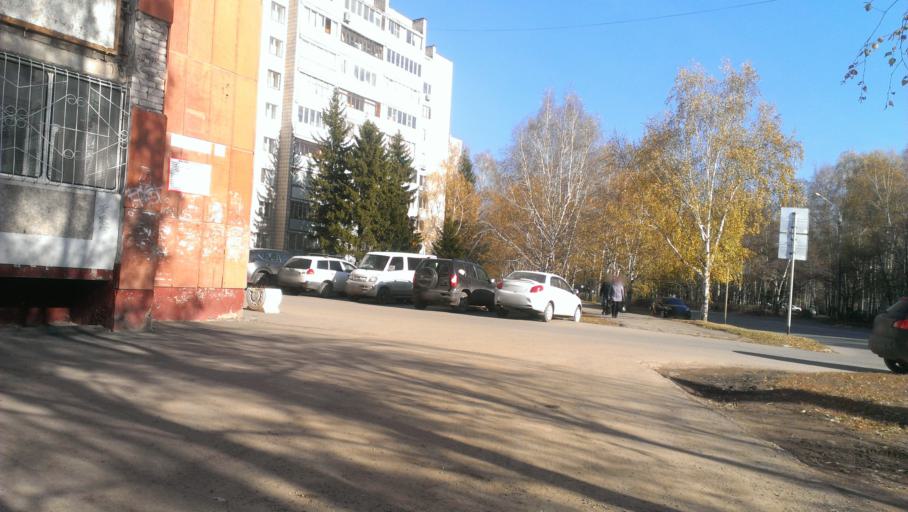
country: RU
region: Altai Krai
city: Novosilikatnyy
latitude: 53.3467
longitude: 83.6802
